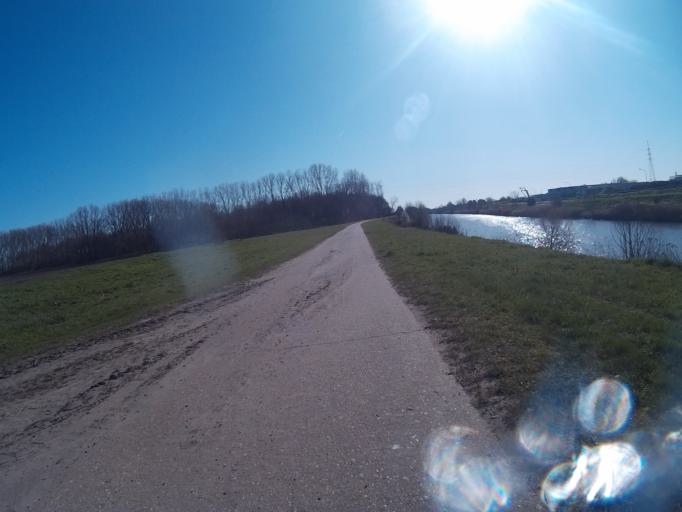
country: BE
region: Flanders
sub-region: Provincie Oost-Vlaanderen
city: Aalter
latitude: 51.1097
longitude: 3.4570
